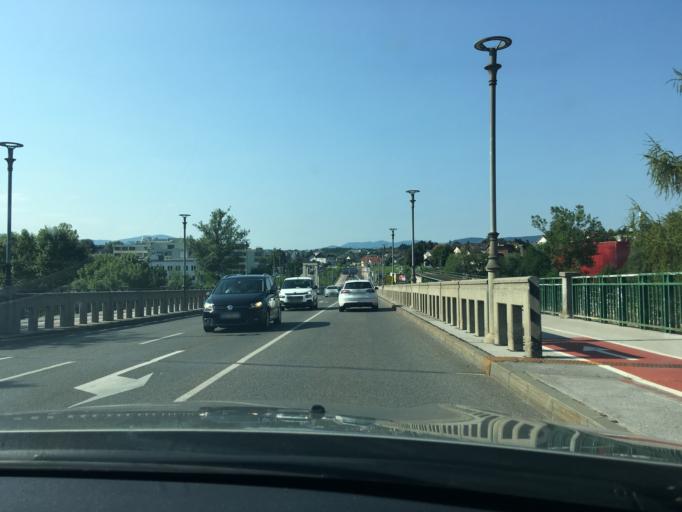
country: SI
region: Novo Mesto
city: Novo Mesto
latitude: 45.8042
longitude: 15.1623
